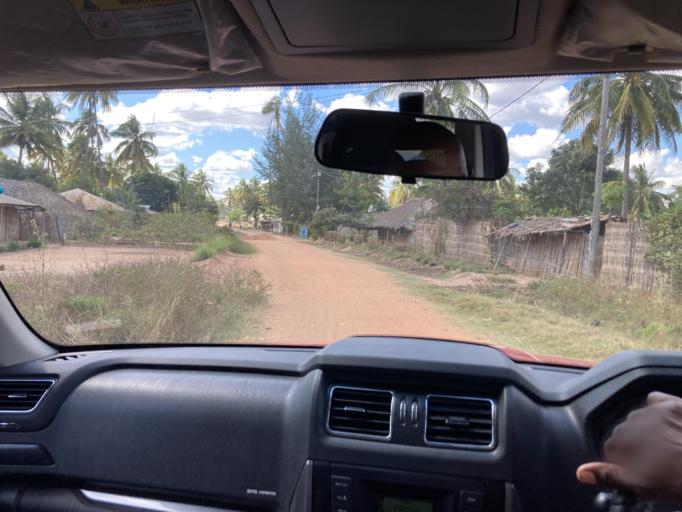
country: MZ
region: Cabo Delgado
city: Montepuez
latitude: -13.1396
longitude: 39.0001
